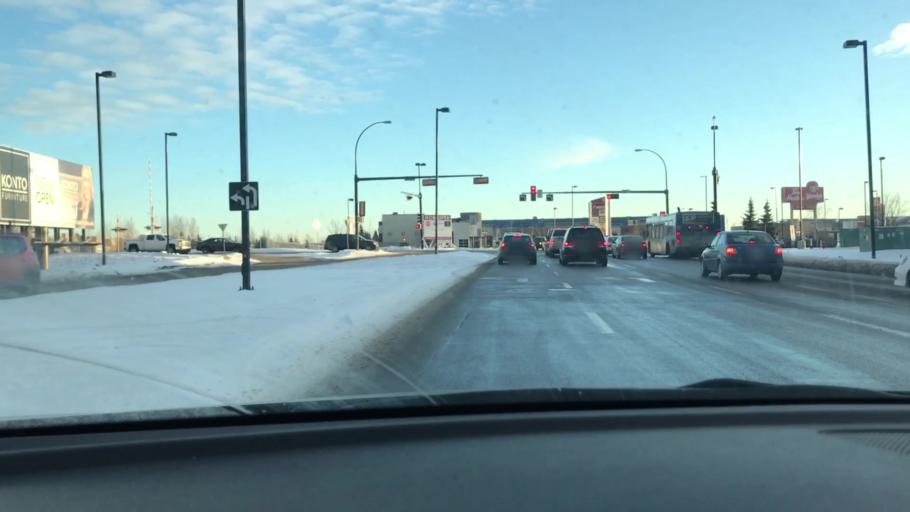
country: CA
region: Alberta
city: Edmonton
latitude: 53.4474
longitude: -113.4907
